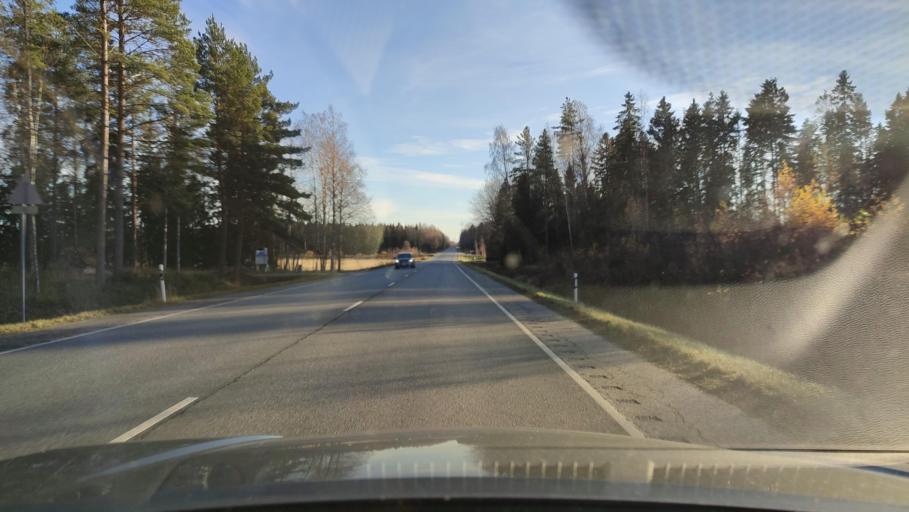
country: FI
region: Ostrobothnia
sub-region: Vaasa
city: Ristinummi
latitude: 63.0092
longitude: 21.7623
